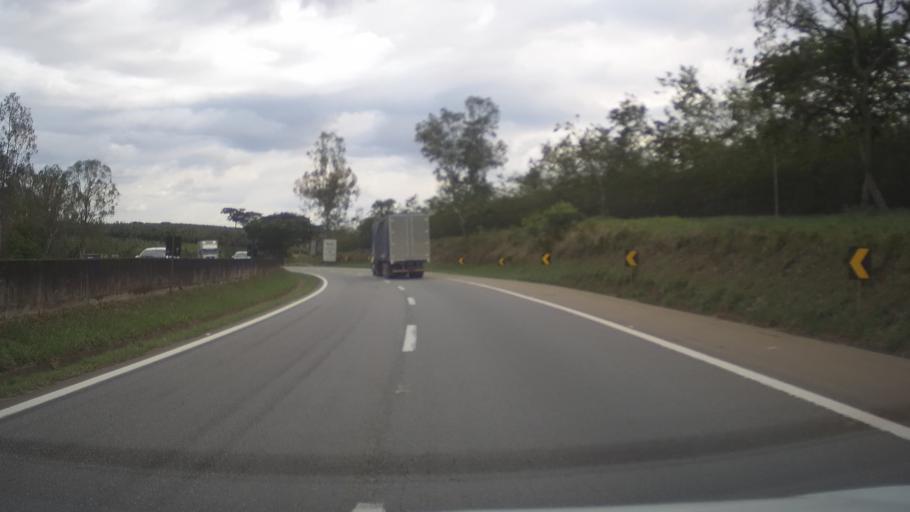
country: BR
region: Minas Gerais
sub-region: Nepomuceno
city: Nepomuceno
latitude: -21.4633
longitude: -45.2057
